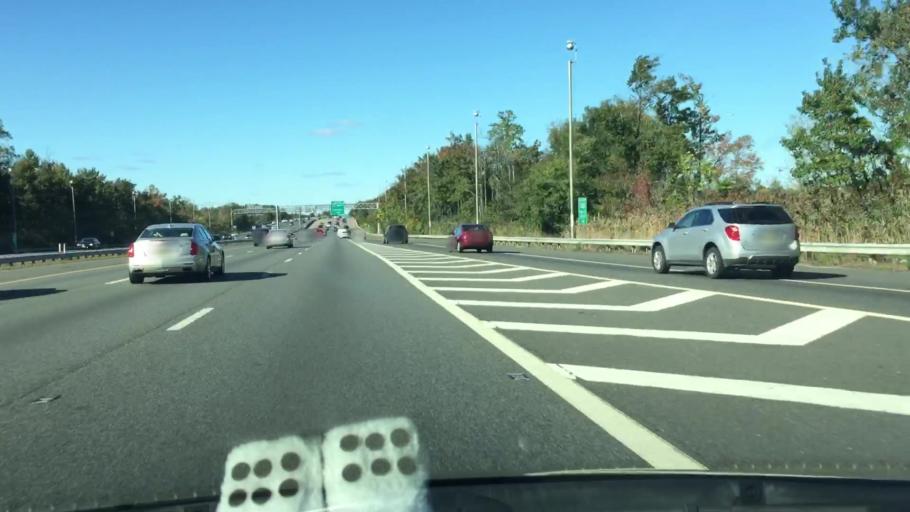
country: US
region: New Jersey
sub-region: Camden County
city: Bellmawr
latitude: 39.8491
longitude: -75.0957
